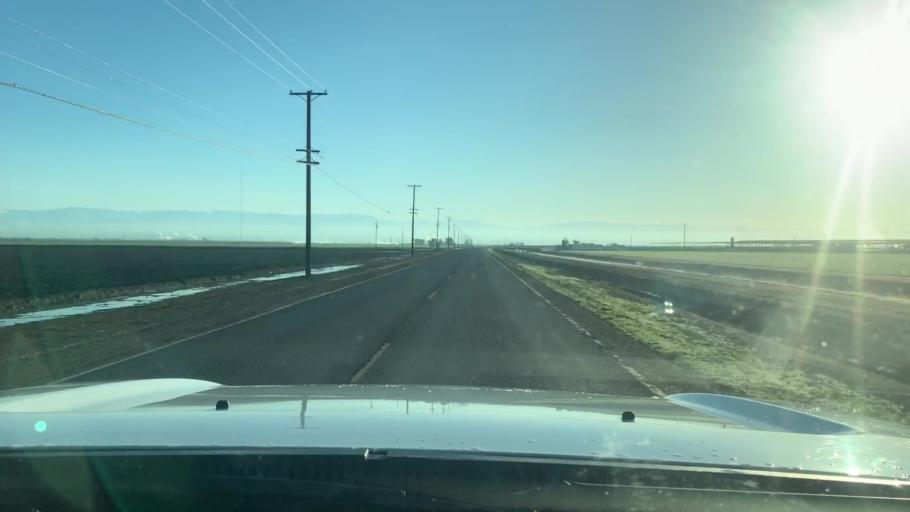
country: US
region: California
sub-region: Tulare County
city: Tulare
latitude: 36.1817
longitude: -119.4145
